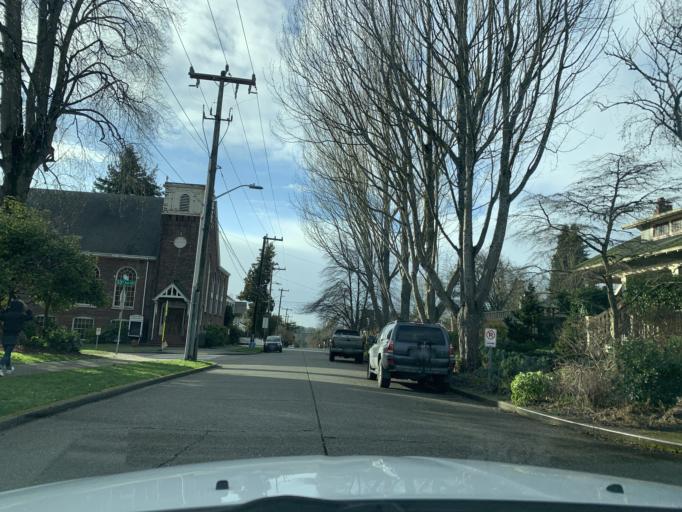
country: US
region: Washington
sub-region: King County
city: Seattle
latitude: 47.6722
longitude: -122.2922
